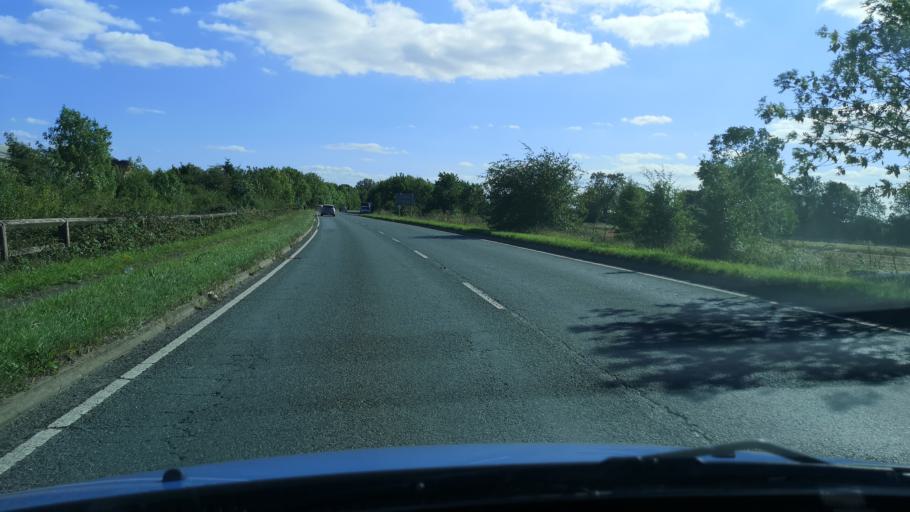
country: GB
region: England
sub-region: North Lincolnshire
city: Belton
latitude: 53.5667
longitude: -0.8188
